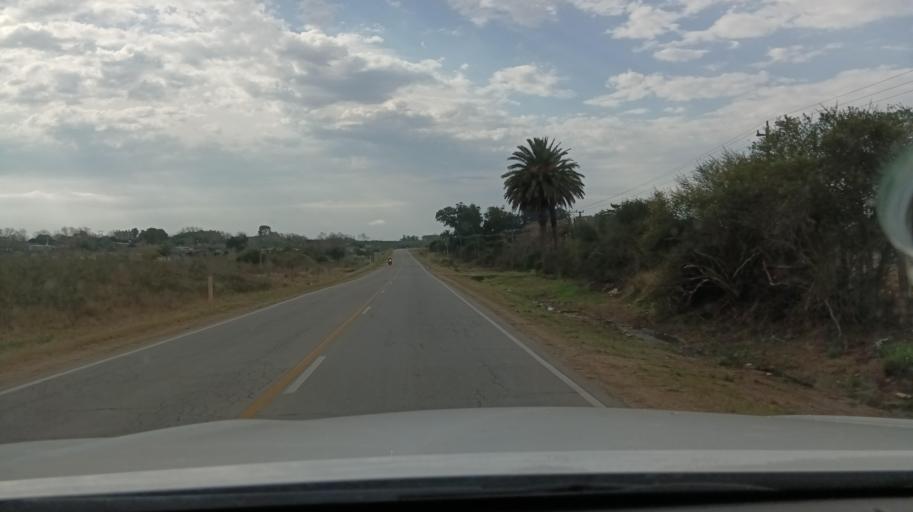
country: UY
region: Canelones
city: Toledo
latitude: -34.7153
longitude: -56.1130
